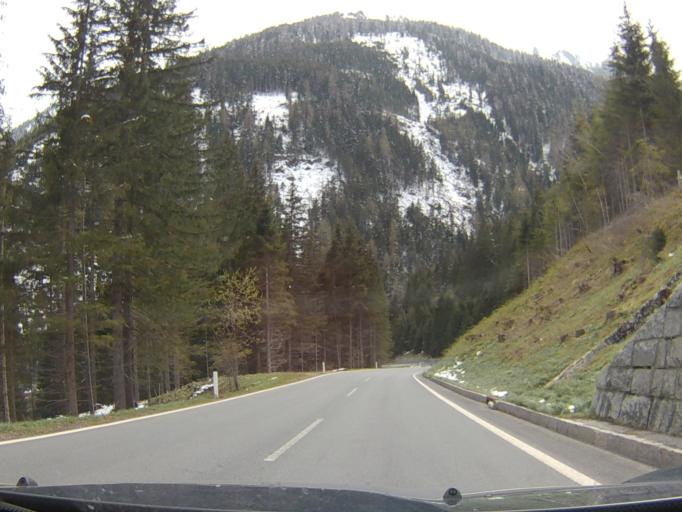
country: AT
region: Salzburg
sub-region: Politischer Bezirk Zell am See
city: Krimml
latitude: 47.2211
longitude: 12.1589
